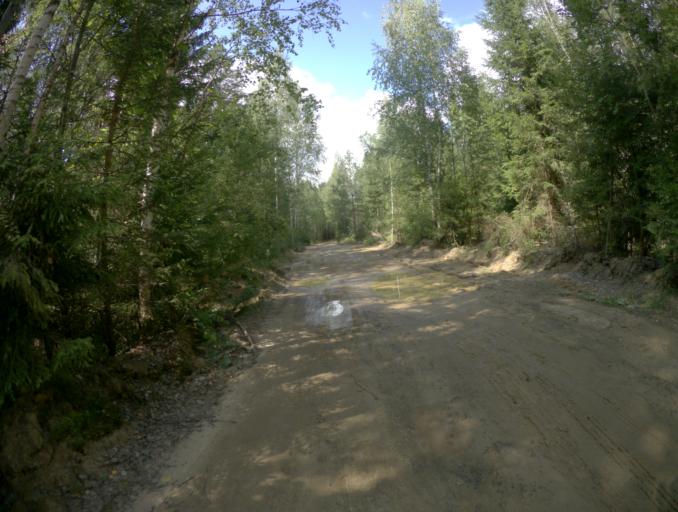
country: RU
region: Vladimir
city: Raduzhnyy
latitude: 55.9671
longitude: 40.2324
